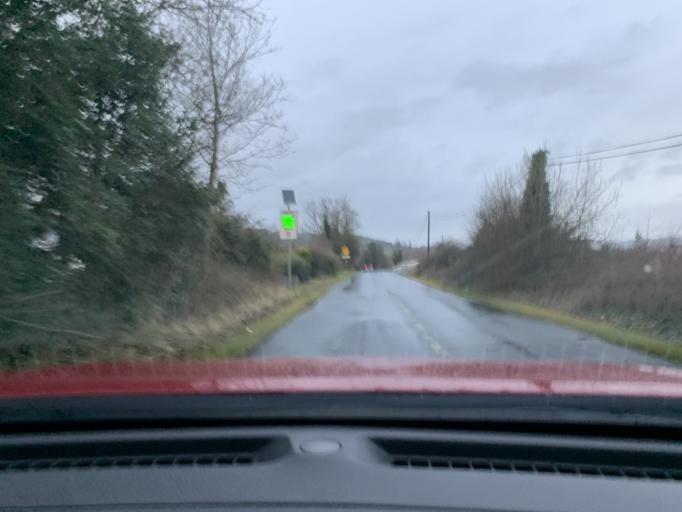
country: IE
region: Connaught
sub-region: Roscommon
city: Boyle
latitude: 54.0235
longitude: -8.3287
